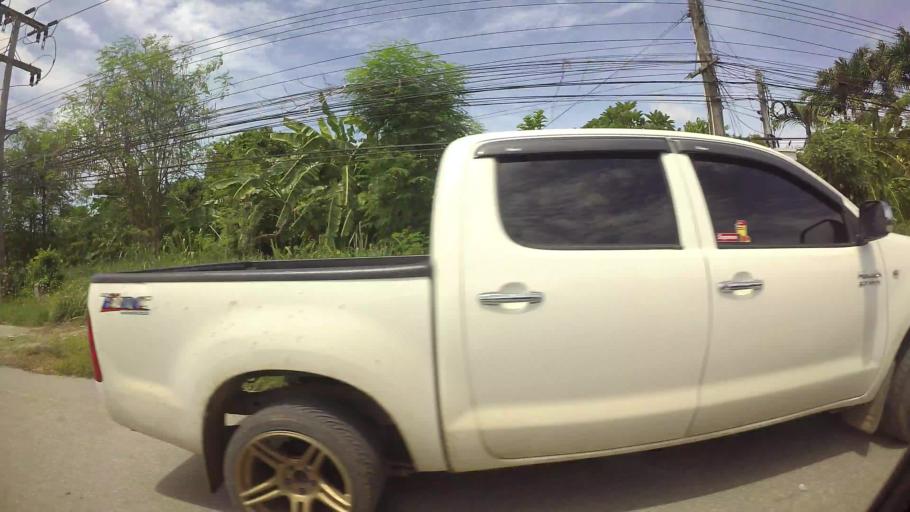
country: TH
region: Chon Buri
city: Sattahip
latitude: 12.7044
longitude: 100.8877
